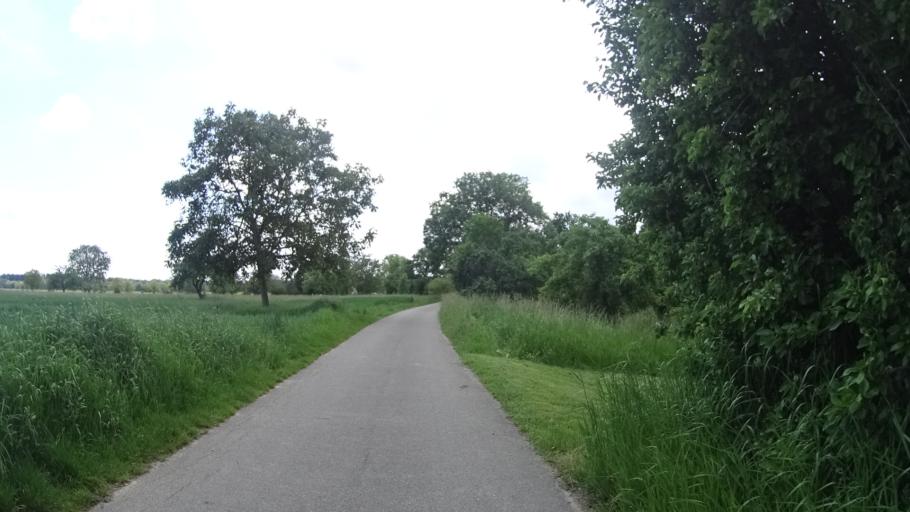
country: DE
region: Baden-Wuerttemberg
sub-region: Freiburg Region
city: Weisweil
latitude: 48.2213
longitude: 7.7051
